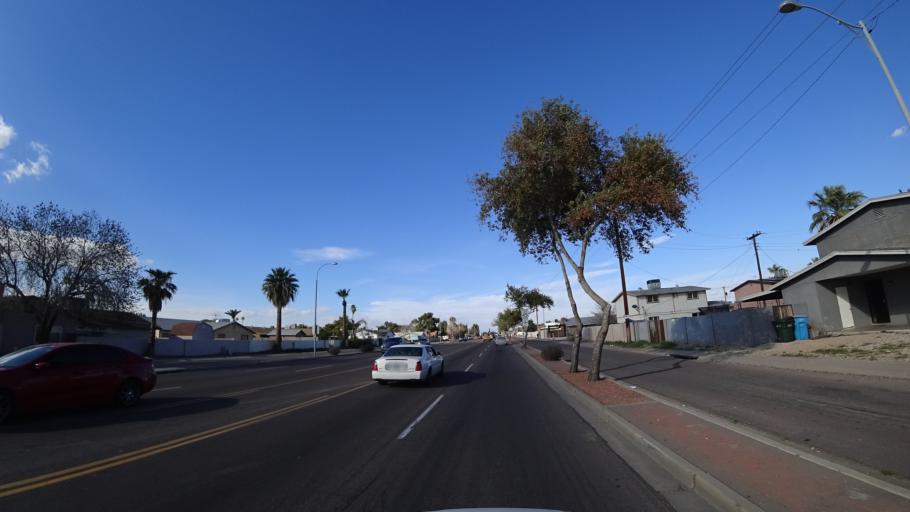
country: US
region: Arizona
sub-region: Maricopa County
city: Tolleson
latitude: 33.4877
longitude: -112.2377
